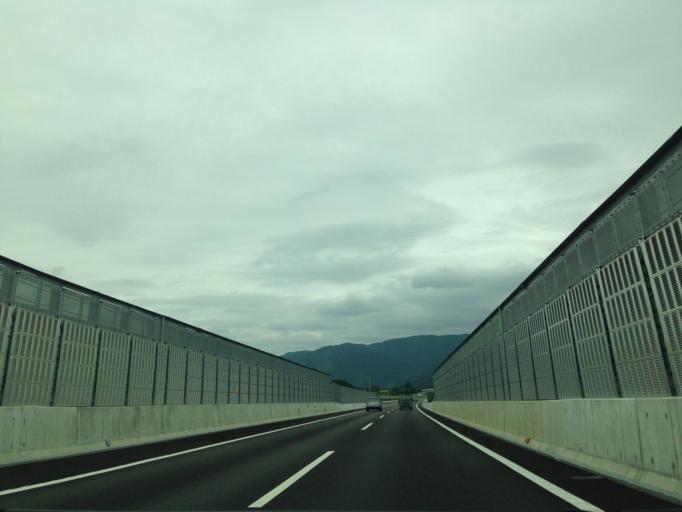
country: JP
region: Aichi
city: Shinshiro
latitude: 34.9202
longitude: 137.5587
